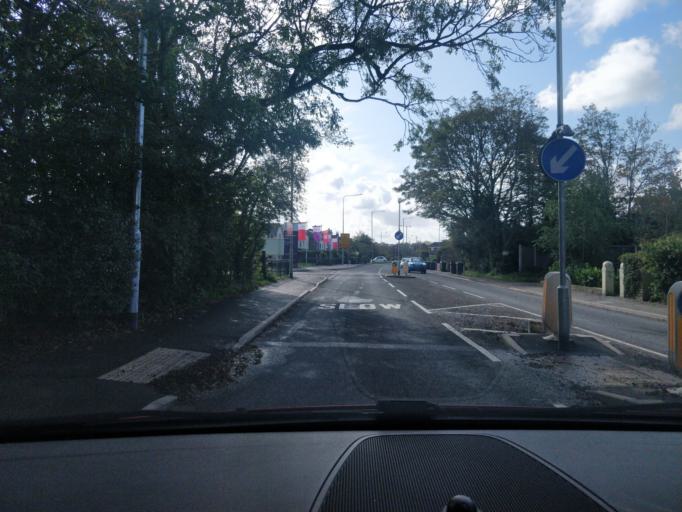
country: GB
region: England
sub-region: Lancashire
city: Ormskirk
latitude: 53.5774
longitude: -2.8765
